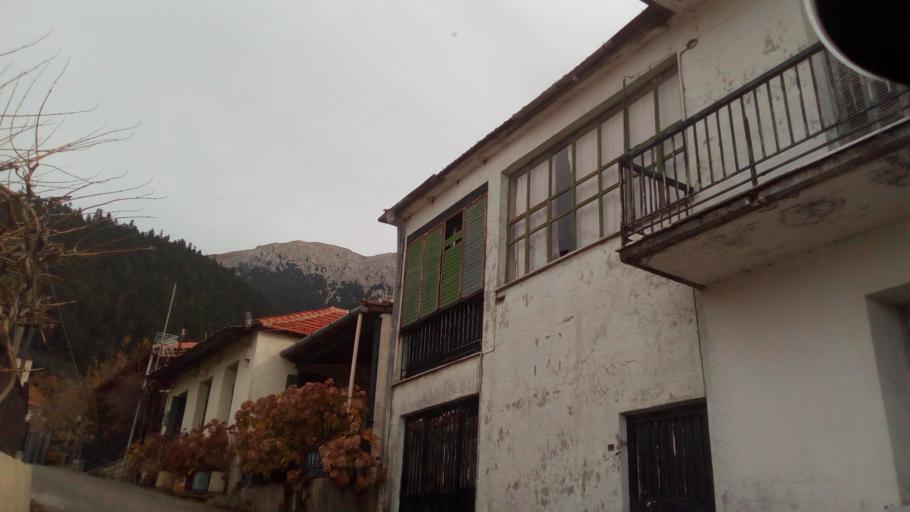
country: GR
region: West Greece
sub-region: Nomos Aitolias kai Akarnanias
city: Thermo
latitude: 38.6850
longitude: 21.8659
